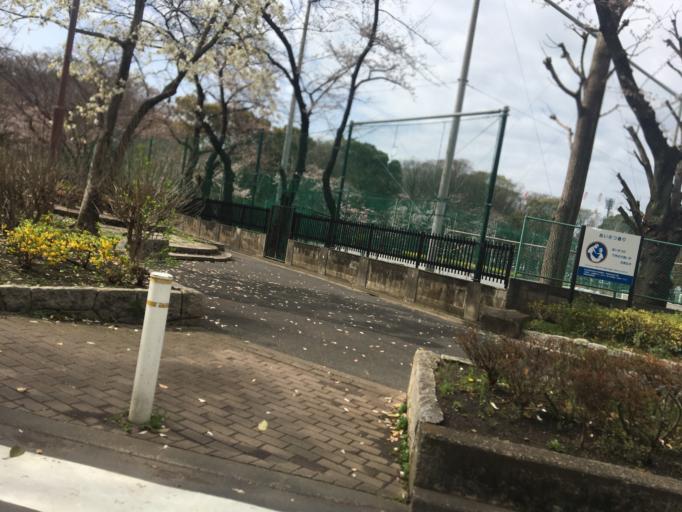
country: JP
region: Saitama
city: Shimotoda
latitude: 35.7563
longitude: 139.6780
